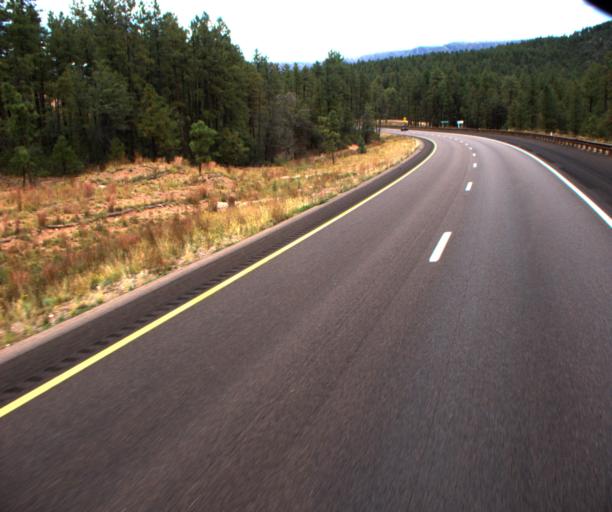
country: US
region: Arizona
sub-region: Gila County
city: Star Valley
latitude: 34.3044
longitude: -111.1091
